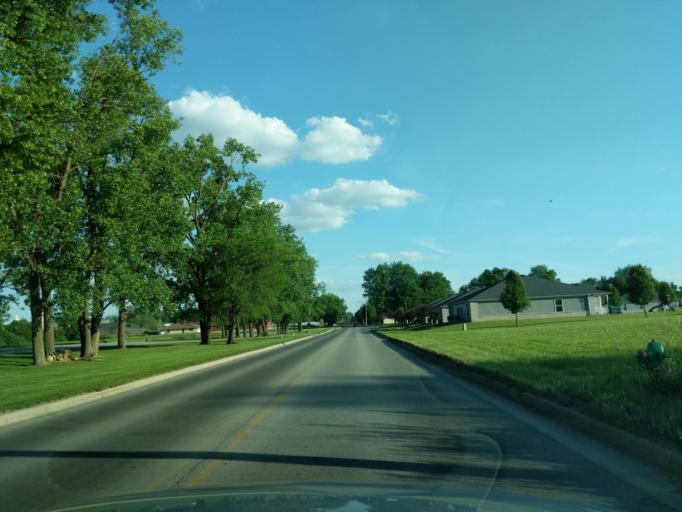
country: US
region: Indiana
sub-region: Huntington County
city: Huntington
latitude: 40.8921
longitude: -85.4712
